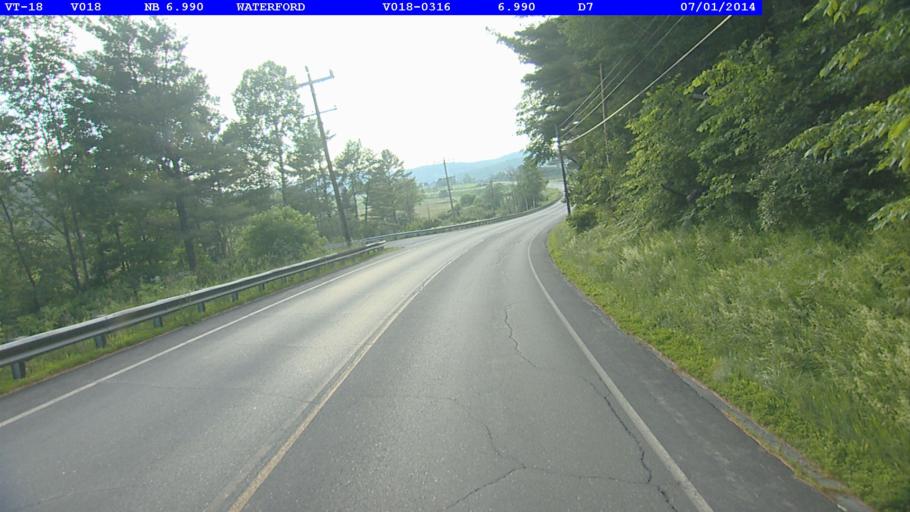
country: US
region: Vermont
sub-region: Caledonia County
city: St Johnsbury
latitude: 44.4232
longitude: -71.9483
